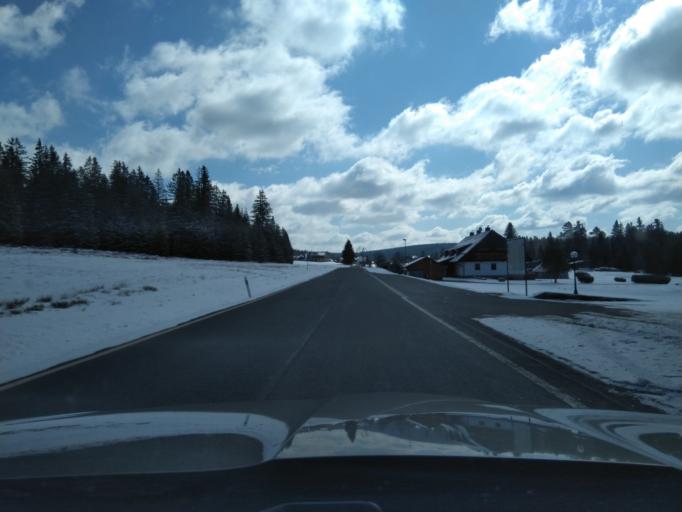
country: CZ
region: Plzensky
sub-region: Okres Klatovy
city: Kasperske Hory
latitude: 49.0543
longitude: 13.5640
